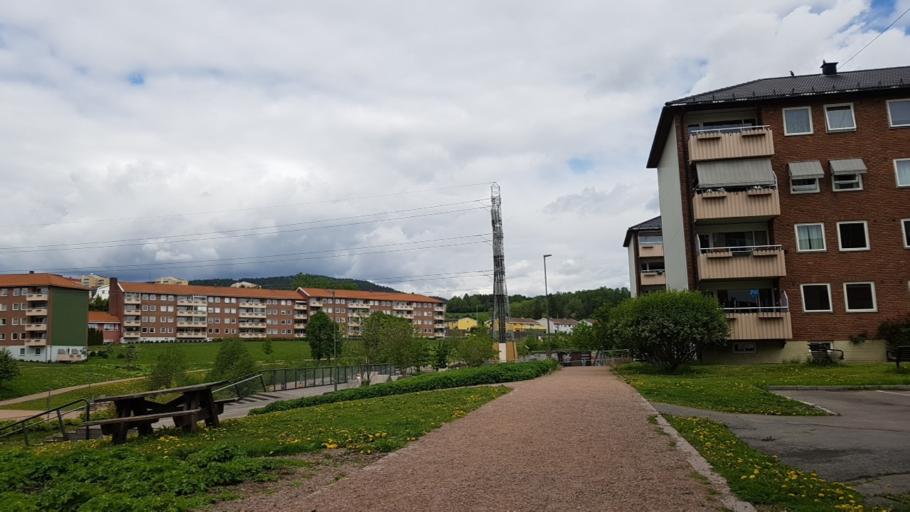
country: NO
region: Oslo
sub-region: Oslo
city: Oslo
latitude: 59.9383
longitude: 10.8225
